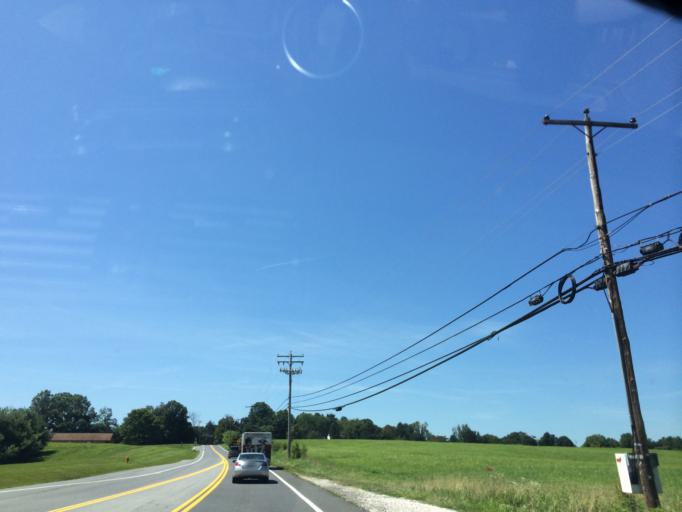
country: US
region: Maryland
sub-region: Howard County
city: Columbia
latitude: 39.3149
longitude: -76.8803
